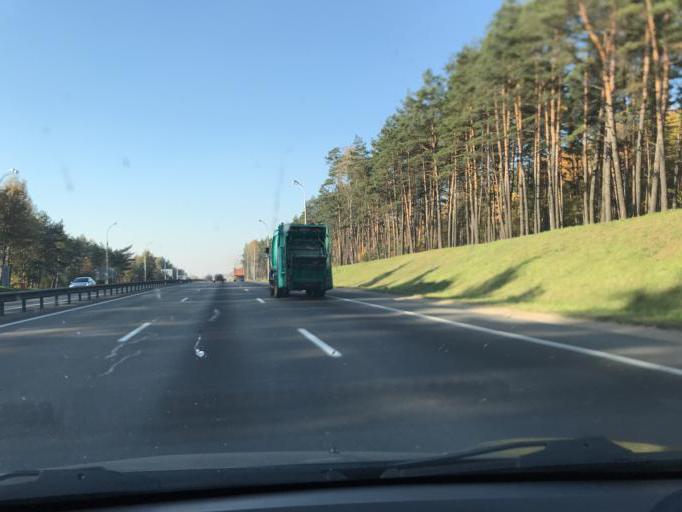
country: BY
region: Minsk
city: Vyaliki Trastsyanets
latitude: 53.8272
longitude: 27.7488
